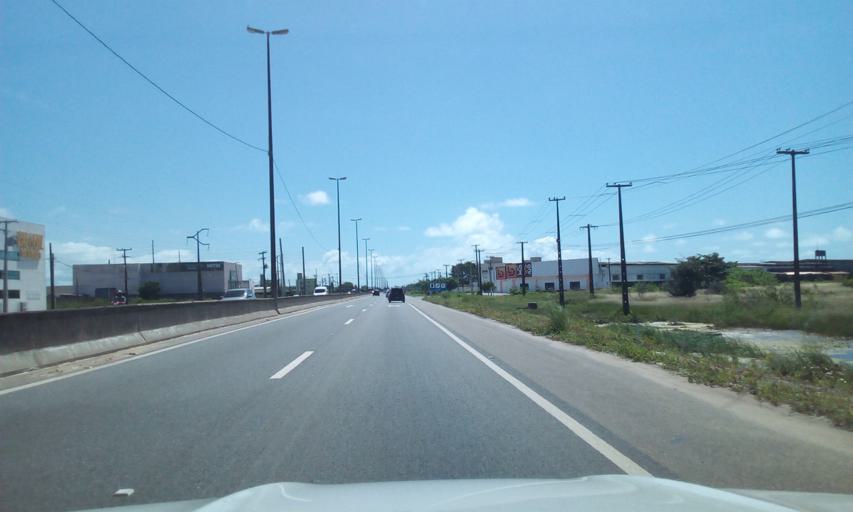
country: BR
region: Paraiba
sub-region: Cabedelo
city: Cabedelo
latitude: -7.0304
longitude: -34.8404
